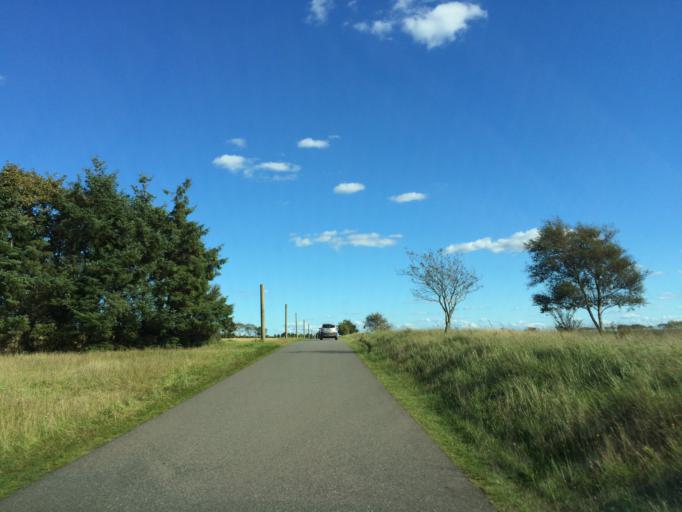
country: DK
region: Central Jutland
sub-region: Holstebro Kommune
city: Holstebro
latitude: 56.2723
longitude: 8.5089
